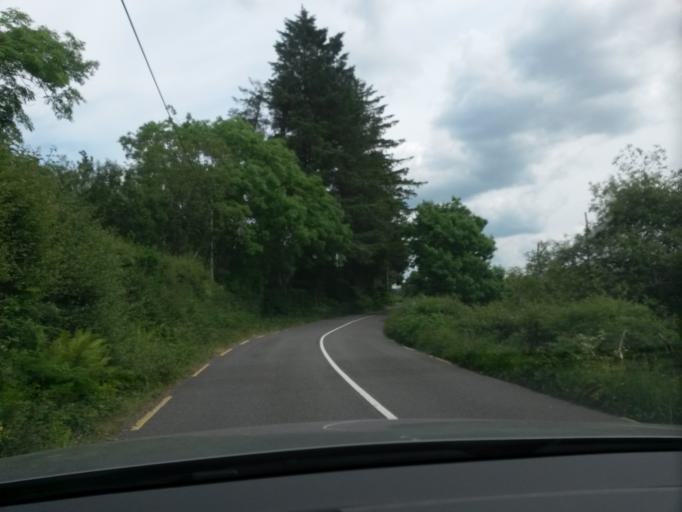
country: IE
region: Munster
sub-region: Ciarrai
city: Kenmare
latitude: 51.9110
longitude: -9.7144
